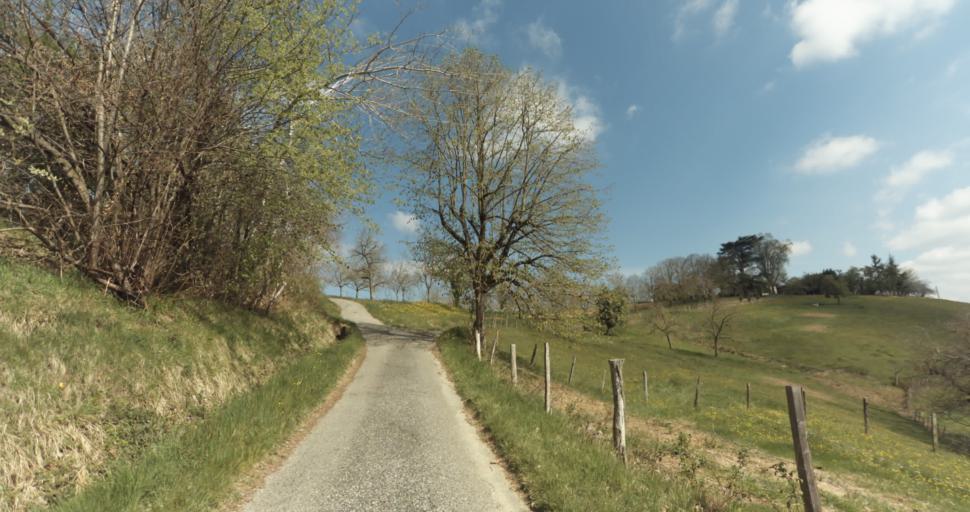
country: FR
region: Rhone-Alpes
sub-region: Departement de l'Isere
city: Saint-Verand
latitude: 45.1740
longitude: 5.3080
